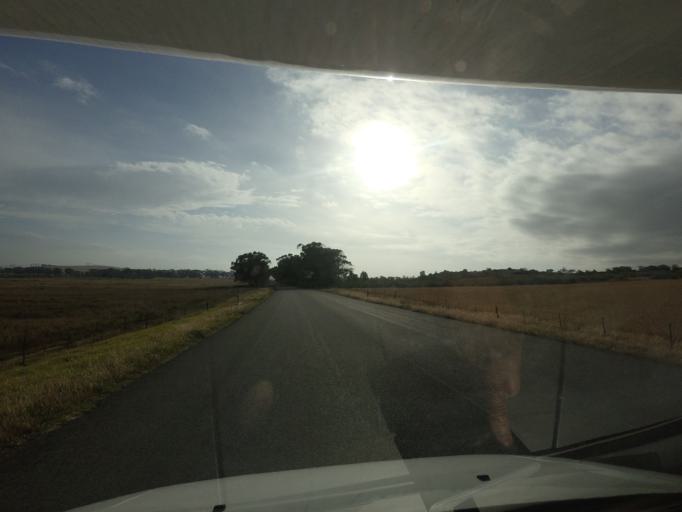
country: ZA
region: Western Cape
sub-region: City of Cape Town
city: Sunset Beach
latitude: -33.7239
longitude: 18.4994
